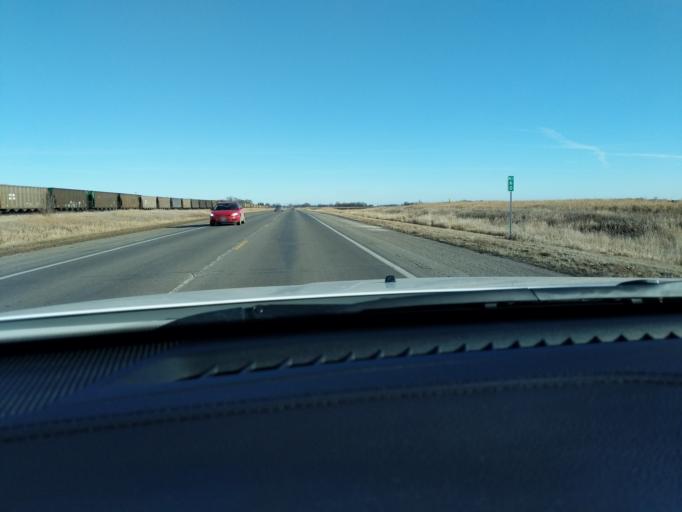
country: US
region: Minnesota
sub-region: Renville County
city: Renville
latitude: 44.7885
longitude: -95.3323
